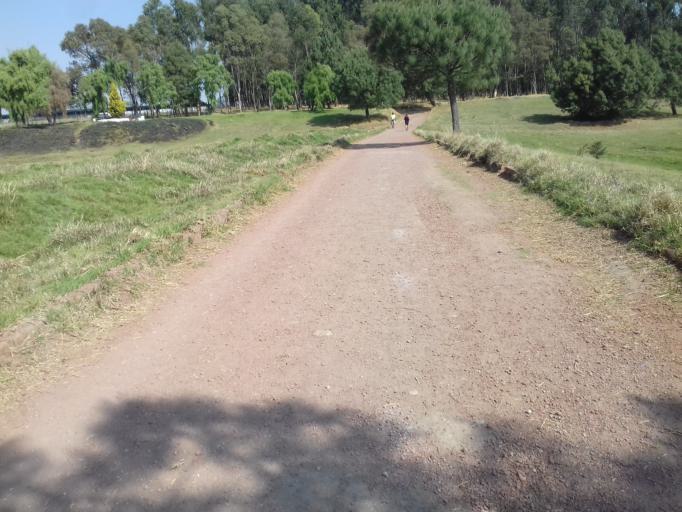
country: MX
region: Mexico
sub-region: Toluca
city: San Antonio Buenavista
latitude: 19.2757
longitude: -99.6970
